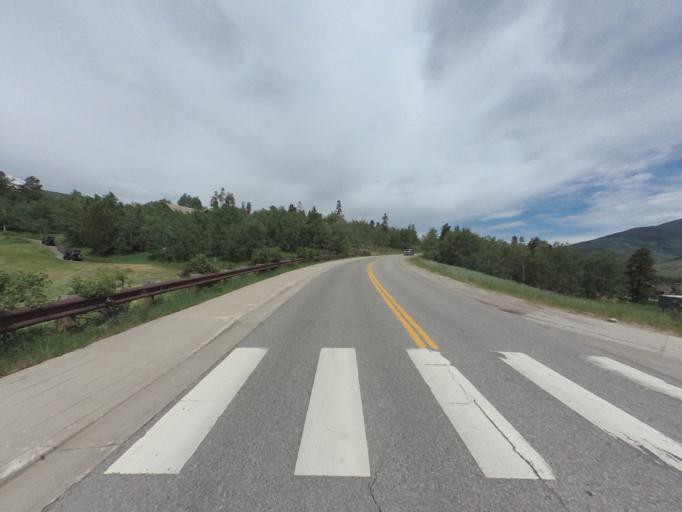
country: US
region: Colorado
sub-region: Summit County
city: Silverthorne
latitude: 39.6545
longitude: -106.0859
